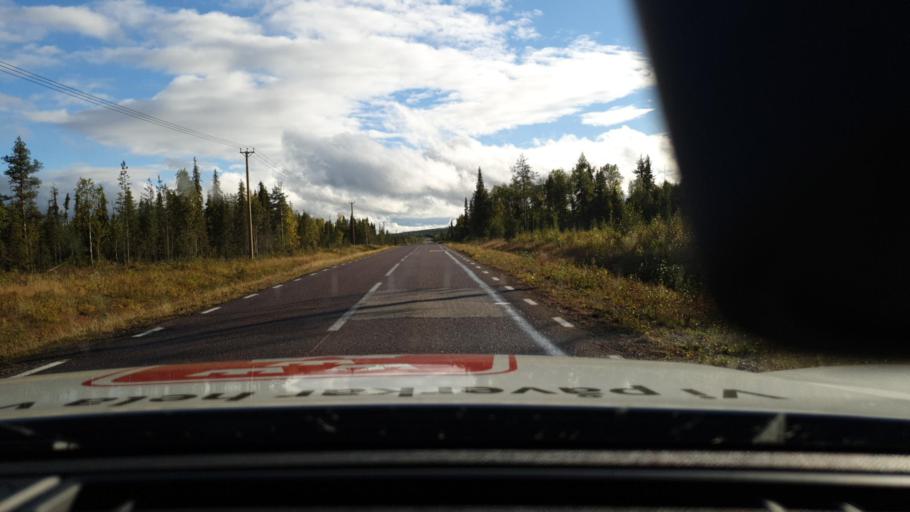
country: SE
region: Norrbotten
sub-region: Overkalix Kommun
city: OEverkalix
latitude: 66.8824
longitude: 22.7653
